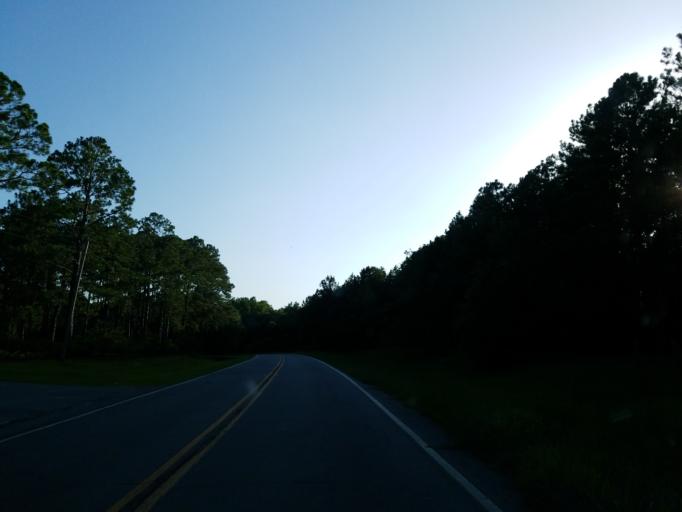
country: US
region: Georgia
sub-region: Ben Hill County
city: Fitzgerald
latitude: 31.7138
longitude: -83.2861
